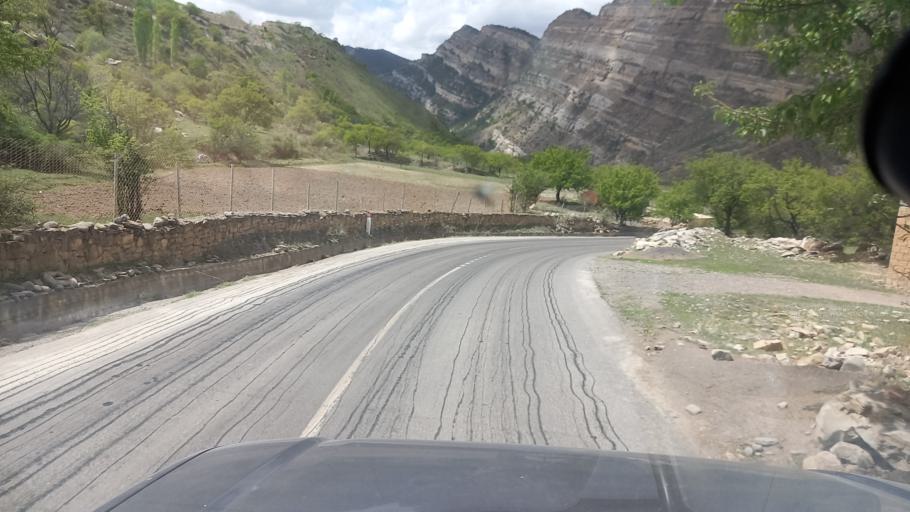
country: RU
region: Dagestan
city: Gunib
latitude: 42.3172
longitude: 46.9245
